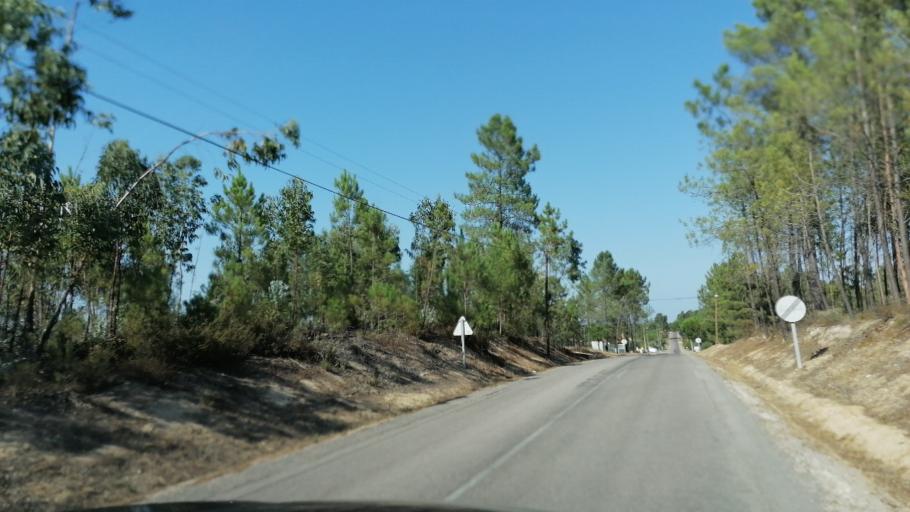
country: PT
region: Evora
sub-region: Vendas Novas
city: Vendas Novas
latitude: 38.7755
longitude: -8.5961
